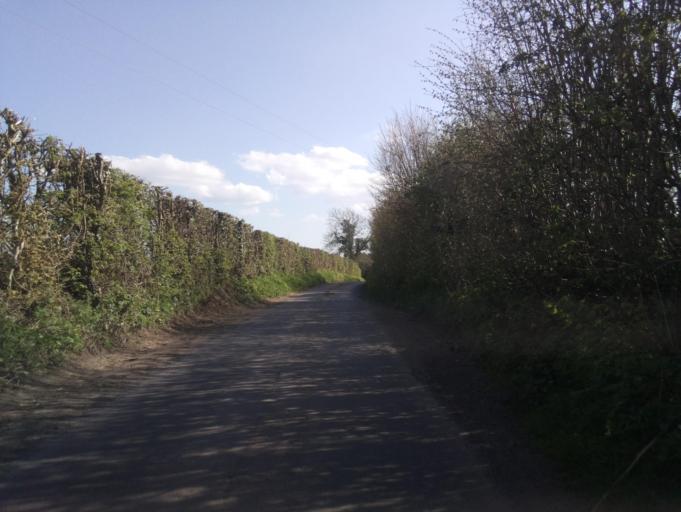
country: GB
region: England
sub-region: South Gloucestershire
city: Alveston
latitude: 51.5996
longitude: -2.5483
